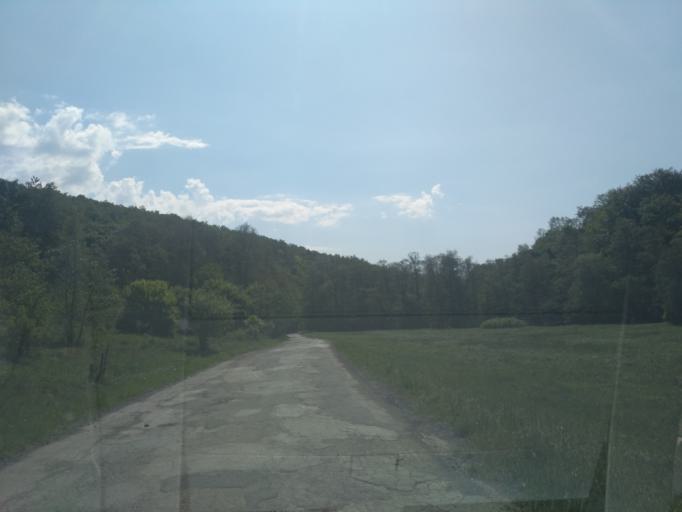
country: SK
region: Kosicky
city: Kosice
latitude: 48.8668
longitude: 21.4181
